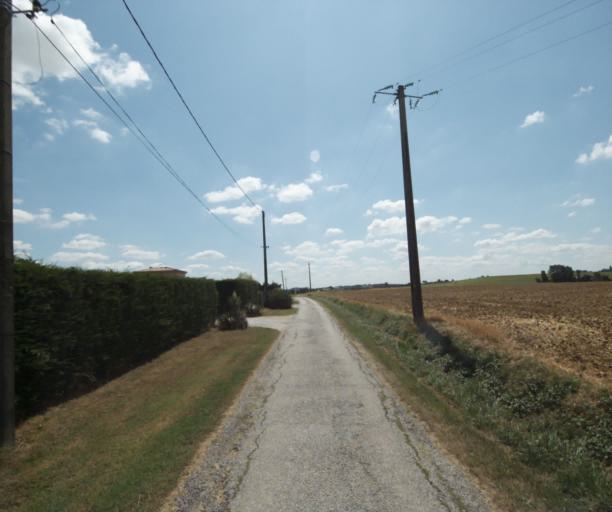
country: FR
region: Midi-Pyrenees
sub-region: Departement de la Haute-Garonne
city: Auriac-sur-Vendinelle
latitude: 43.4711
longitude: 1.8347
